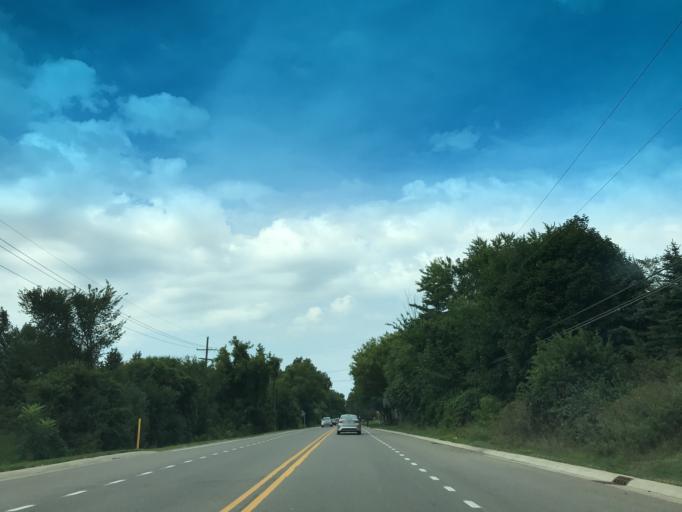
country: US
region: Michigan
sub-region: Oakland County
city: Milford
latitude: 42.5734
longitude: -83.6132
